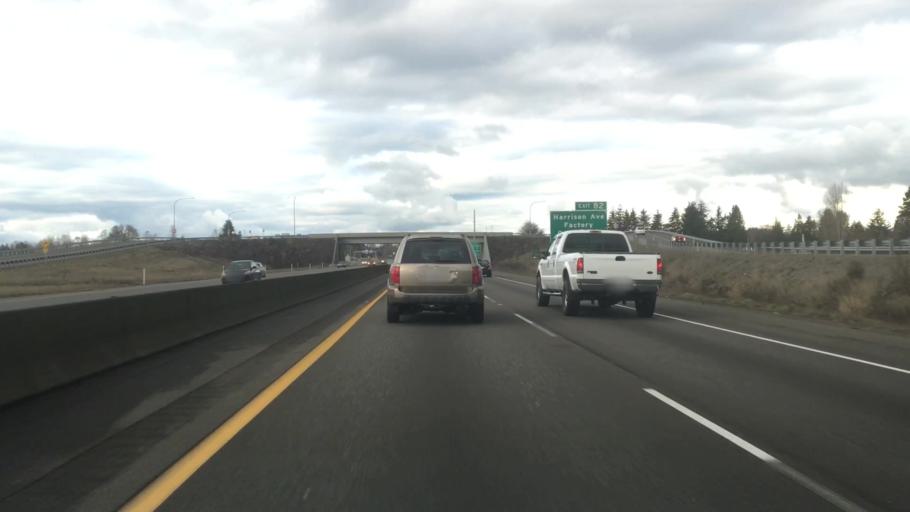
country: US
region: Washington
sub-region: Lewis County
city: Centralia
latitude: 46.7045
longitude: -122.9732
